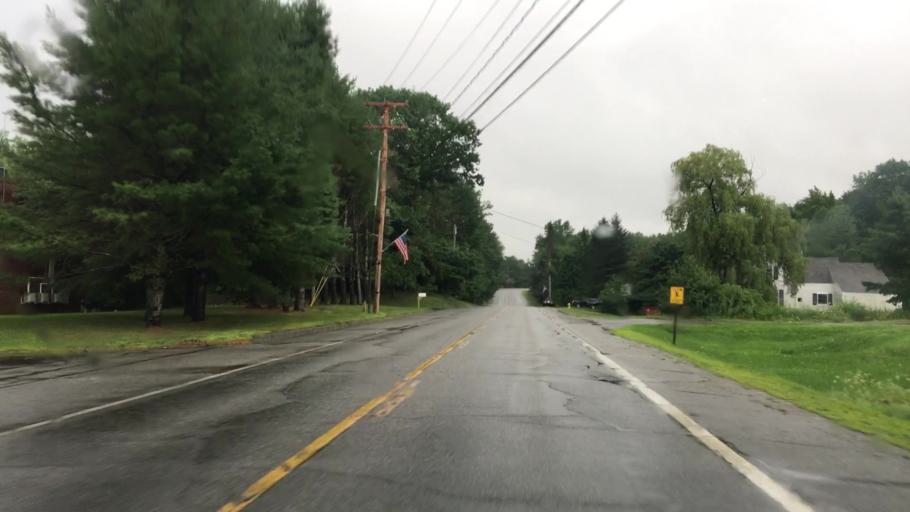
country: US
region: Maine
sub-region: Kennebec County
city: Pittston
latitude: 44.1936
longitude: -69.7598
